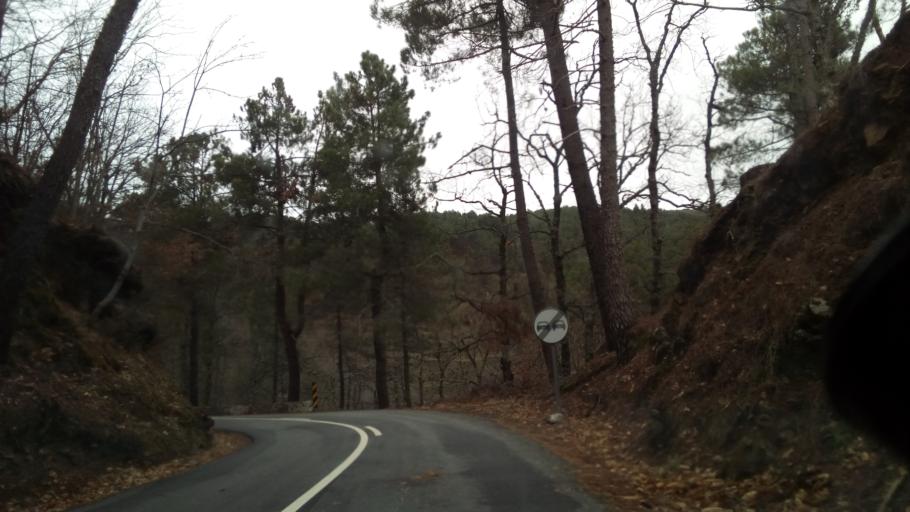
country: PT
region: Guarda
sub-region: Manteigas
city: Manteigas
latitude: 40.4093
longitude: -7.5309
